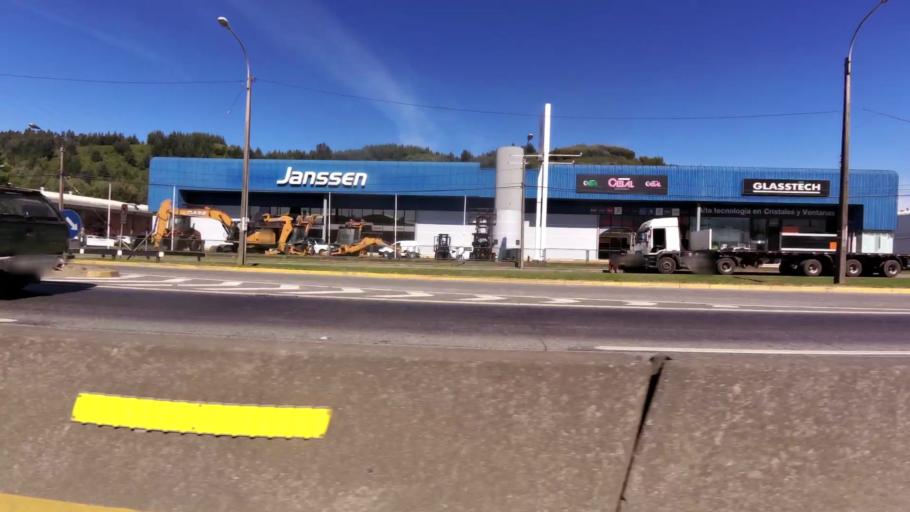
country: CL
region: Biobio
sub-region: Provincia de Concepcion
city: Concepcion
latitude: -36.8082
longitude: -73.0250
